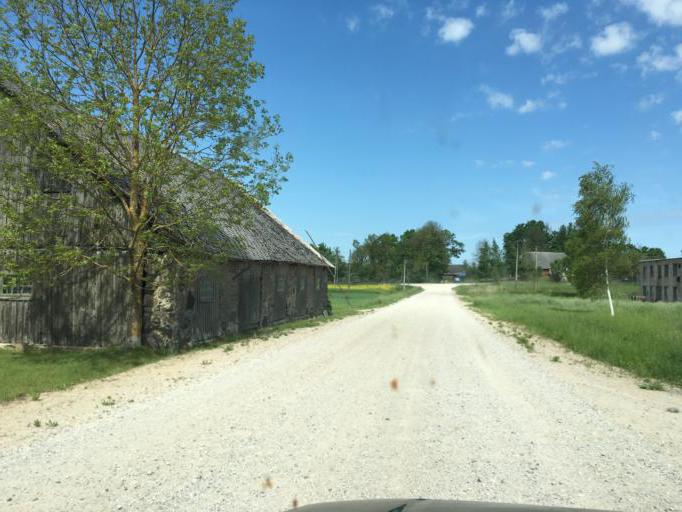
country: LV
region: Talsu Rajons
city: Valdemarpils
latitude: 57.3754
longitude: 22.6189
